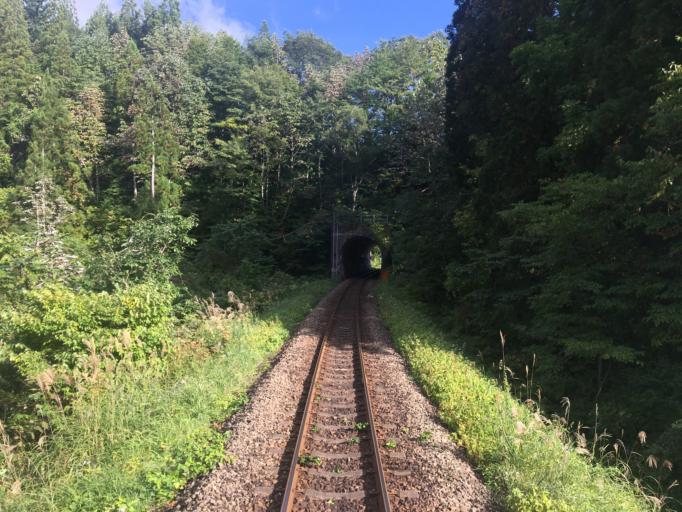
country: JP
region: Akita
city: Kakunodatemachi
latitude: 39.8647
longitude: 140.5763
